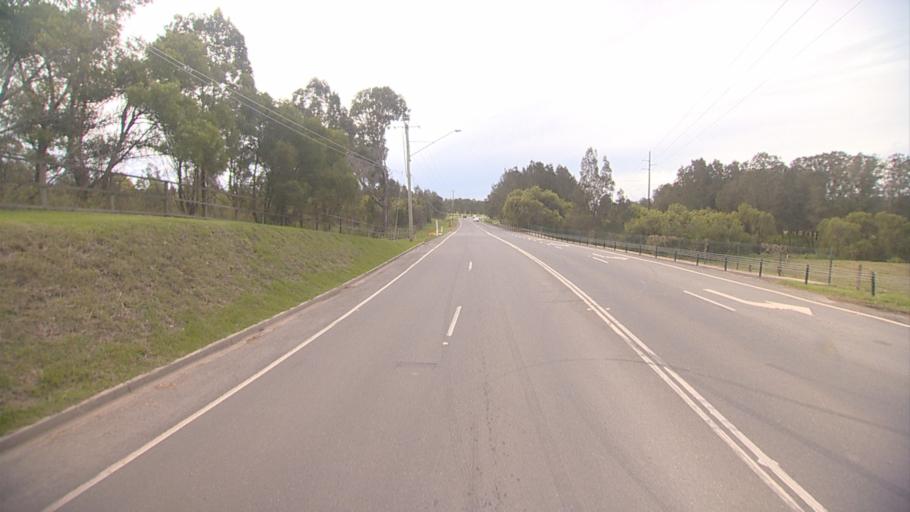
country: AU
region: Queensland
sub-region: Logan
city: Waterford West
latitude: -27.6996
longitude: 153.1181
